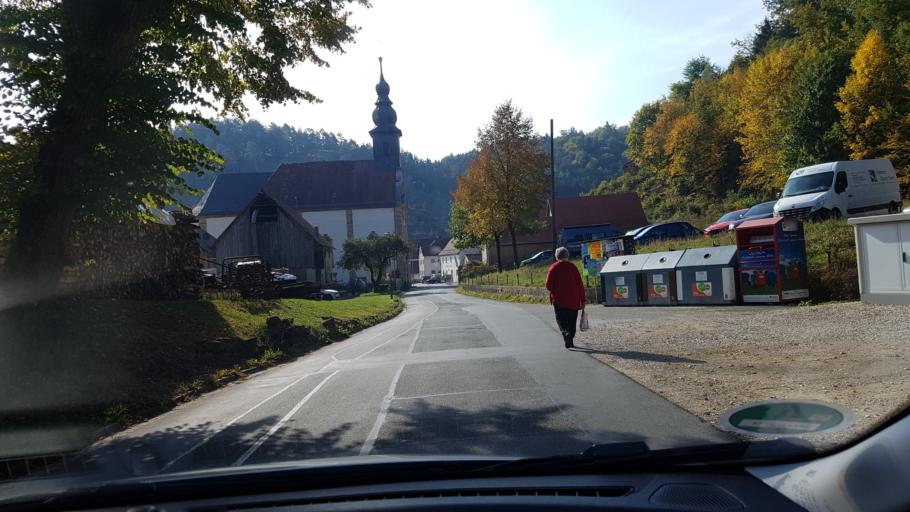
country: DE
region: Bavaria
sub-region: Upper Franconia
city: Waischenfeld
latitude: 49.8139
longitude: 11.3534
